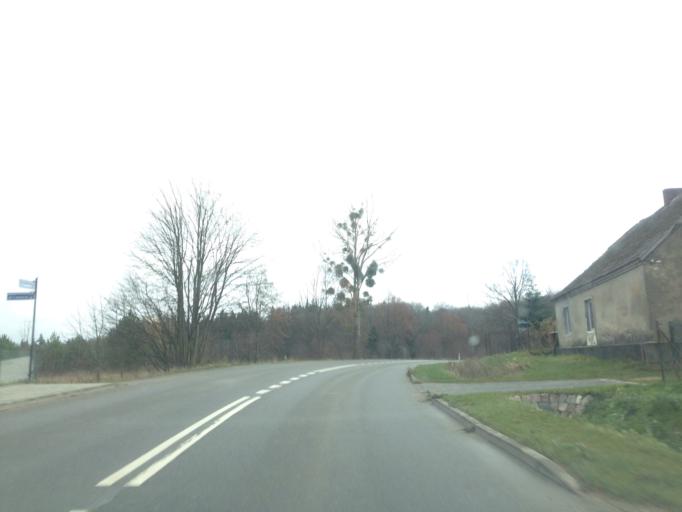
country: PL
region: Pomeranian Voivodeship
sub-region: Powiat gdanski
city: Kolbudy
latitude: 54.2490
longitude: 18.3870
